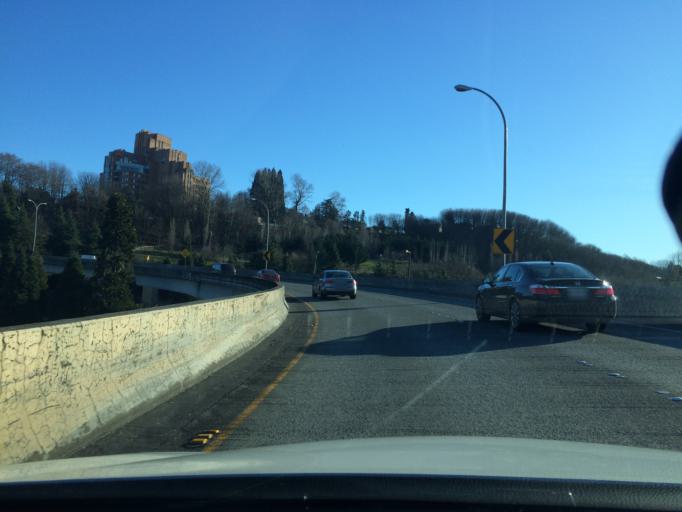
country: US
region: Washington
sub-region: King County
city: Seattle
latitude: 47.5950
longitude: -122.3207
